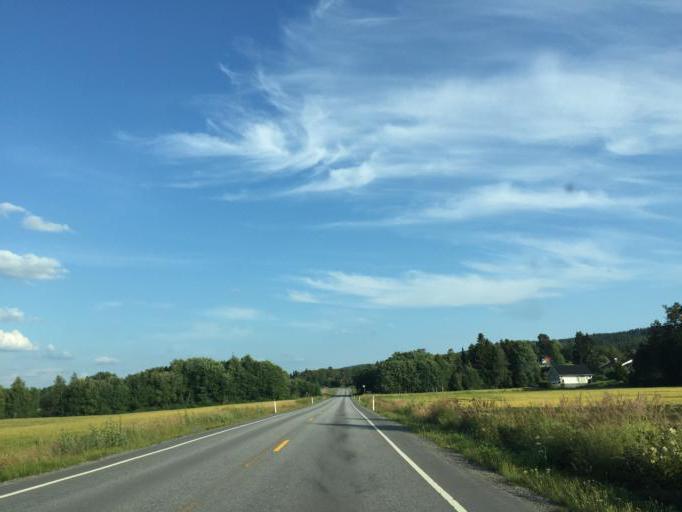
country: NO
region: Hedmark
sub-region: Sor-Odal
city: Skarnes
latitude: 60.2436
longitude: 11.7105
